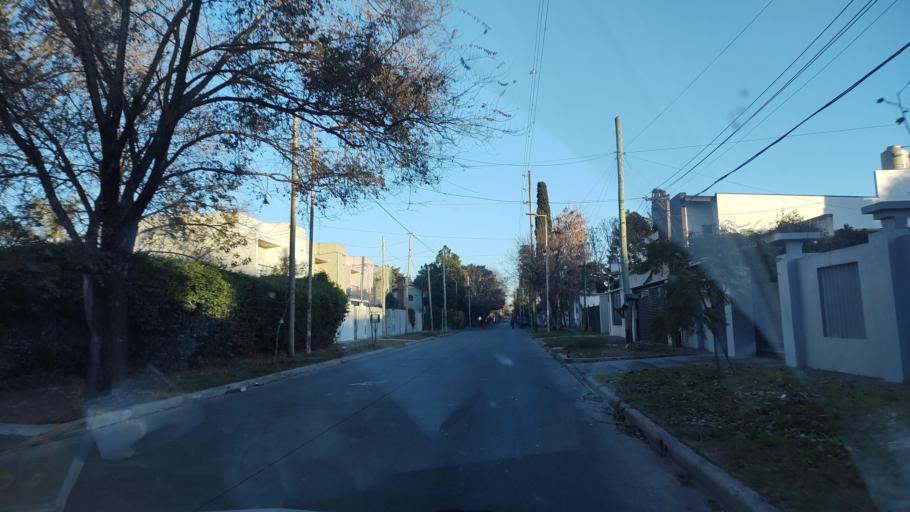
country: AR
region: Buenos Aires
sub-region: Partido de La Plata
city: La Plata
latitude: -34.8905
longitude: -58.0283
